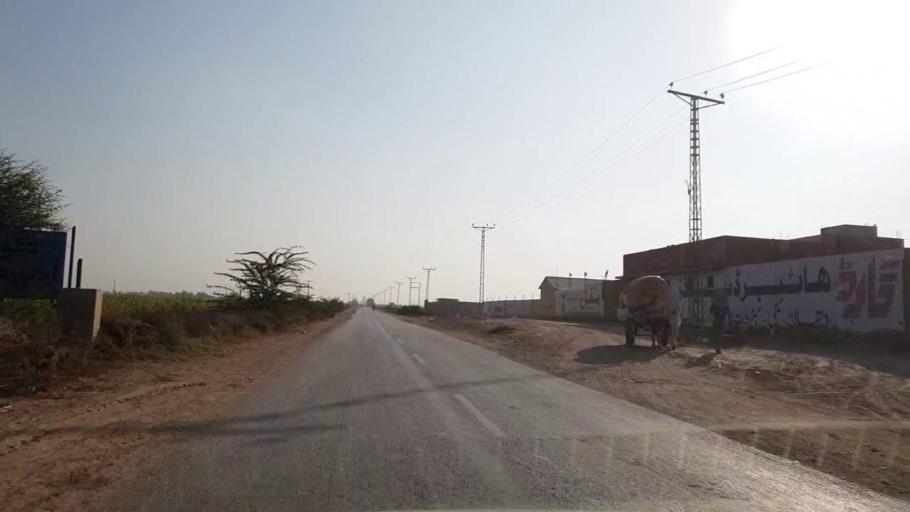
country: PK
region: Sindh
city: Bulri
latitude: 24.8538
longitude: 68.3279
